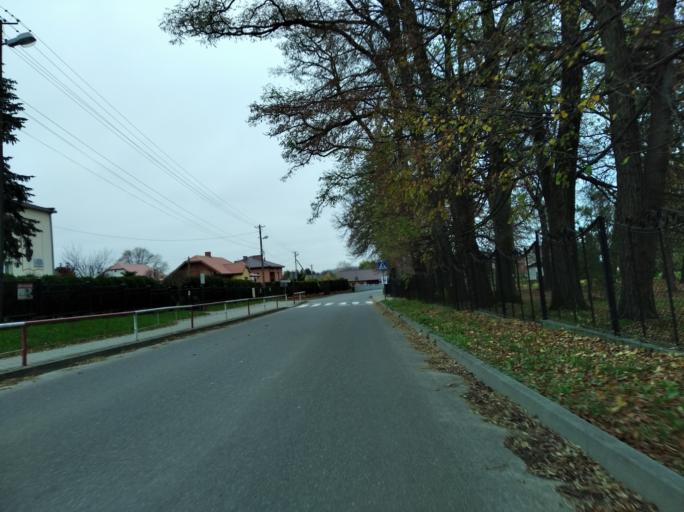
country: PL
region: Subcarpathian Voivodeship
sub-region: Powiat krosnienski
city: Jedlicze
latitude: 49.6918
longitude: 21.6660
